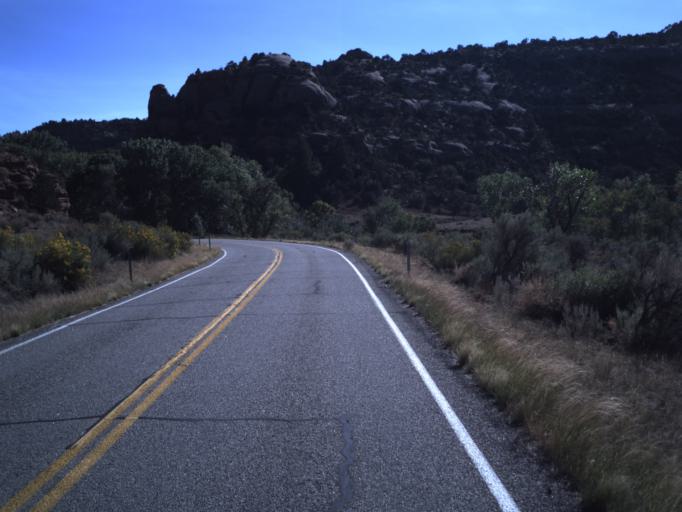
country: US
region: Utah
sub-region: San Juan County
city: Monticello
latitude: 38.0229
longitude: -109.5406
